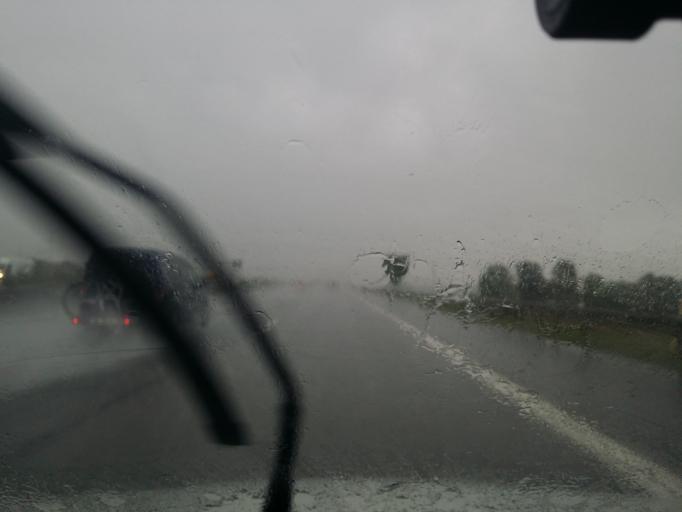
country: DE
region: Thuringia
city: Nohra
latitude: 50.9505
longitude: 11.2298
